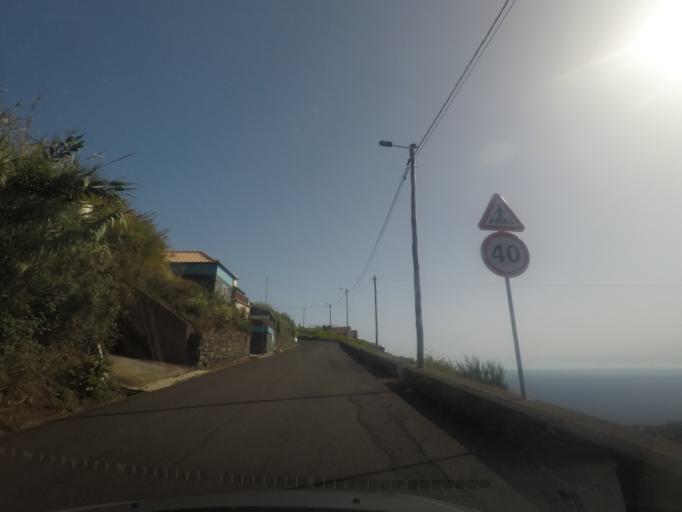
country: PT
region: Madeira
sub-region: Calheta
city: Arco da Calheta
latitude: 32.7278
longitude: -17.1606
